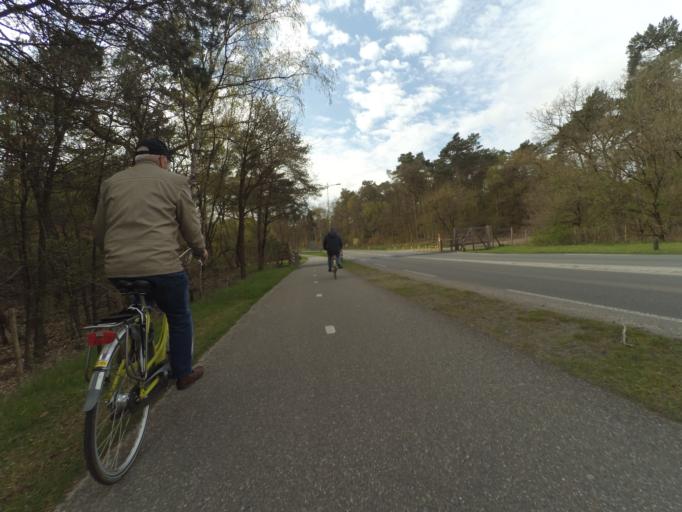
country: NL
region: Gelderland
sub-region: Gemeente Nunspeet
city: Nunspeet
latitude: 52.3609
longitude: 5.7862
